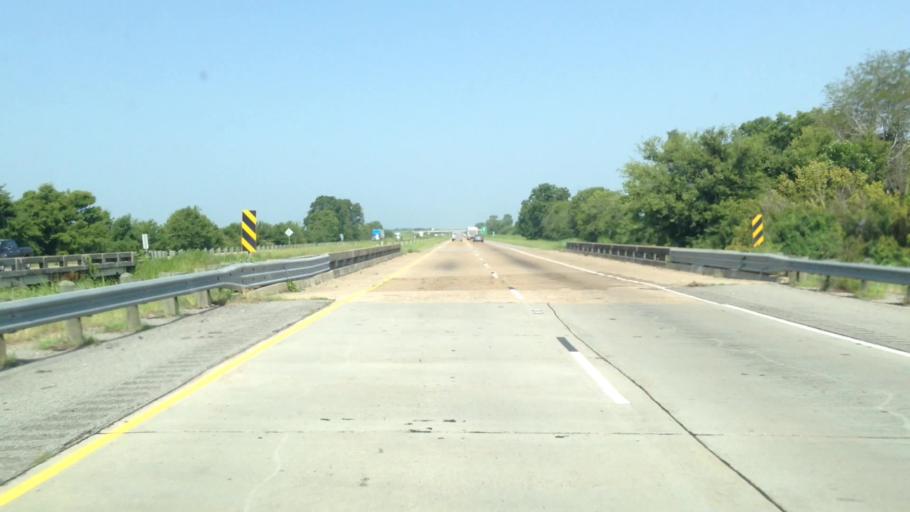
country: US
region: Mississippi
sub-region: Warren County
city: Vicksburg
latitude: 32.3279
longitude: -91.0116
